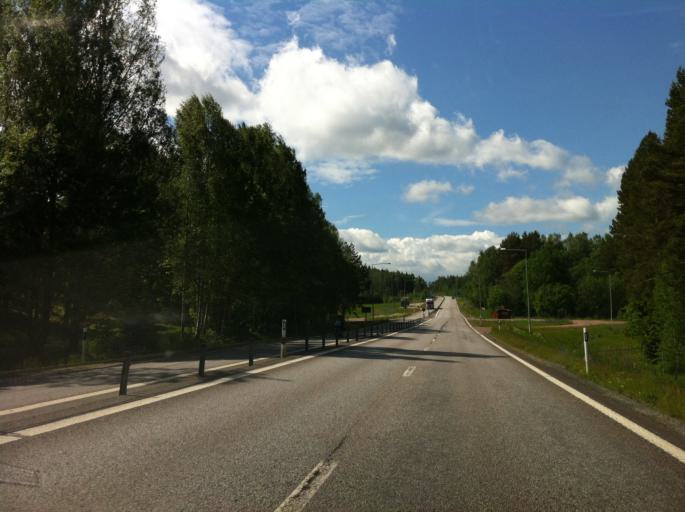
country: SE
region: Vaermland
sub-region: Grums Kommun
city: Slottsbron
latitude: 59.3098
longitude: 13.0850
